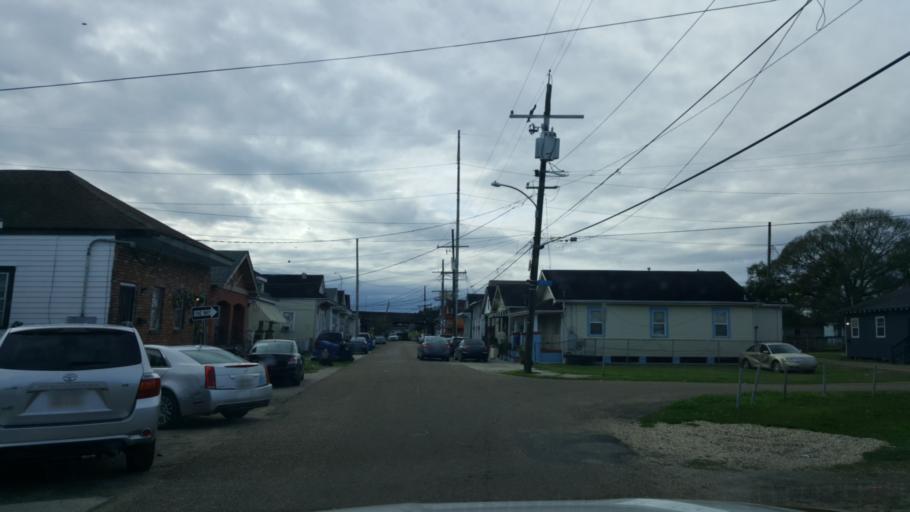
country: US
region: Louisiana
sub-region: Orleans Parish
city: New Orleans
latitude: 29.9762
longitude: -90.0645
